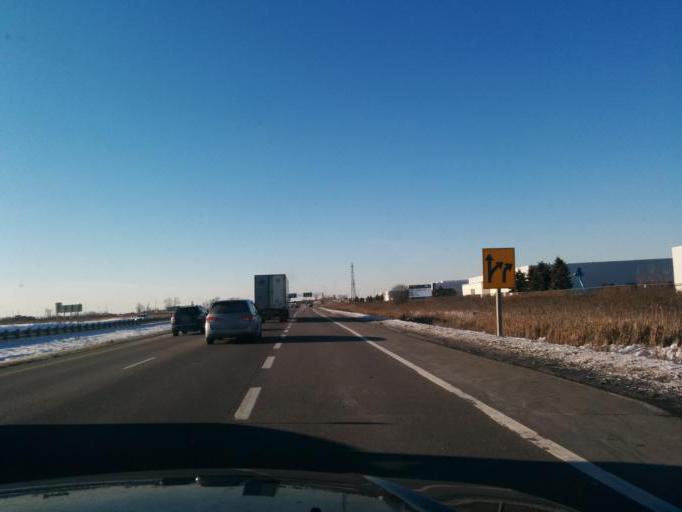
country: CA
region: Ontario
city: Oakville
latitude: 43.5071
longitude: -79.6850
